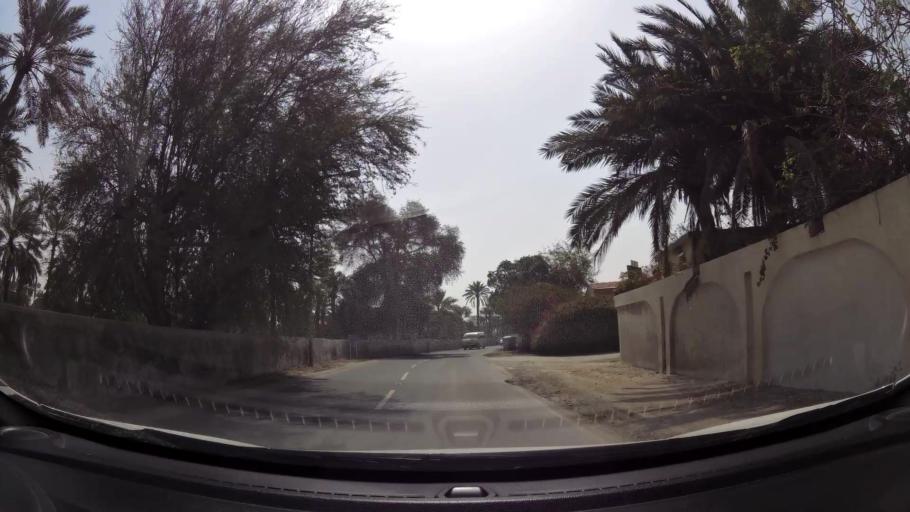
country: BH
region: Manama
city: Jidd Hafs
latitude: 26.2269
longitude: 50.5036
